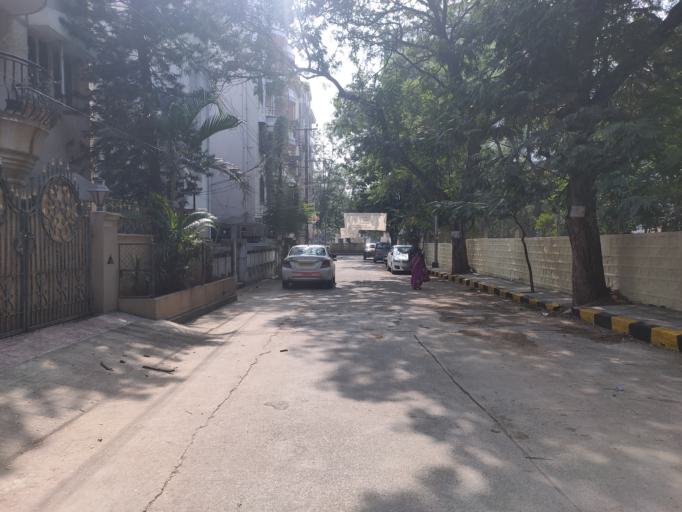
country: IN
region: Telangana
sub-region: Hyderabad
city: Malkajgiri
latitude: 17.4388
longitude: 78.4835
